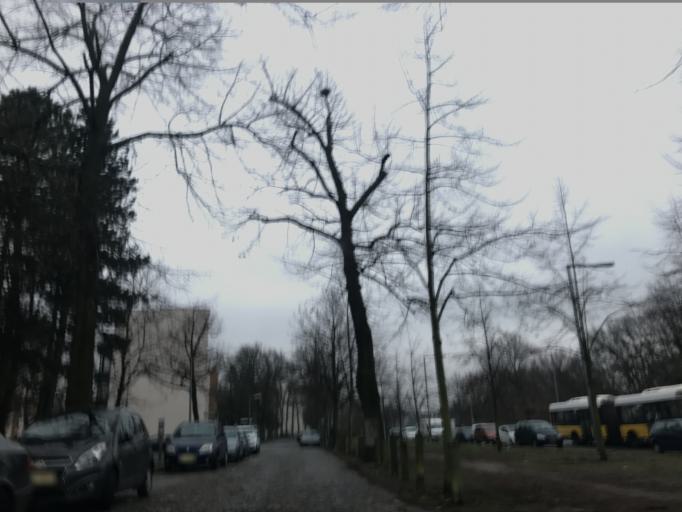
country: DE
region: Berlin
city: Haselhorst
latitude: 52.5439
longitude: 13.2324
